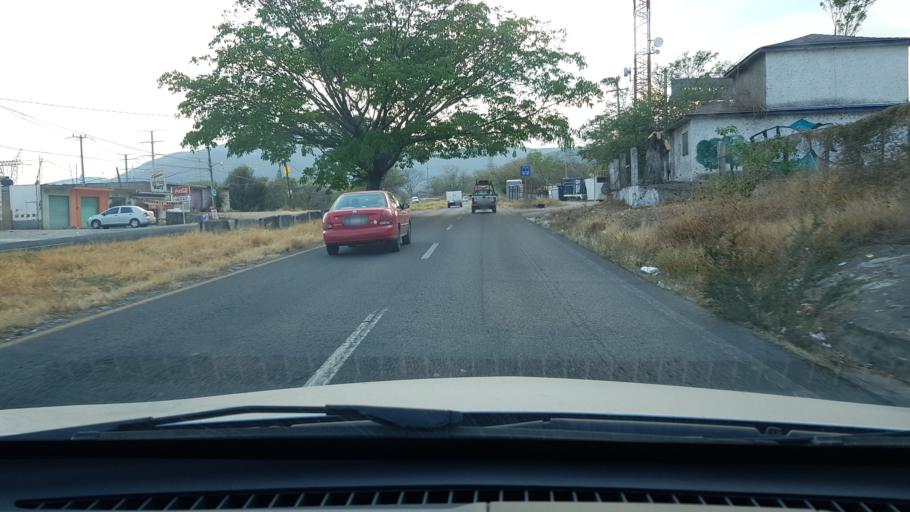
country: MX
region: Morelos
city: Yautepec
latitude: 18.8643
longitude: -99.0930
